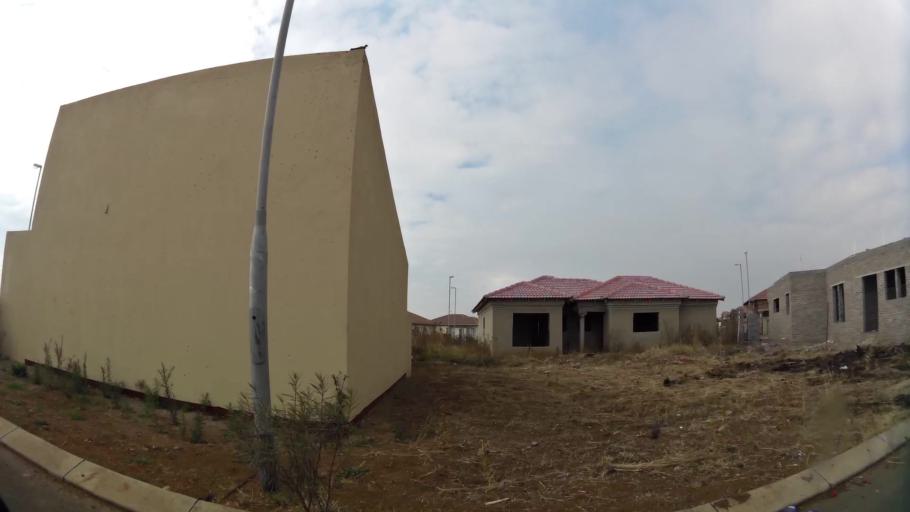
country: ZA
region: Gauteng
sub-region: Sedibeng District Municipality
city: Vanderbijlpark
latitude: -26.6827
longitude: 27.8500
